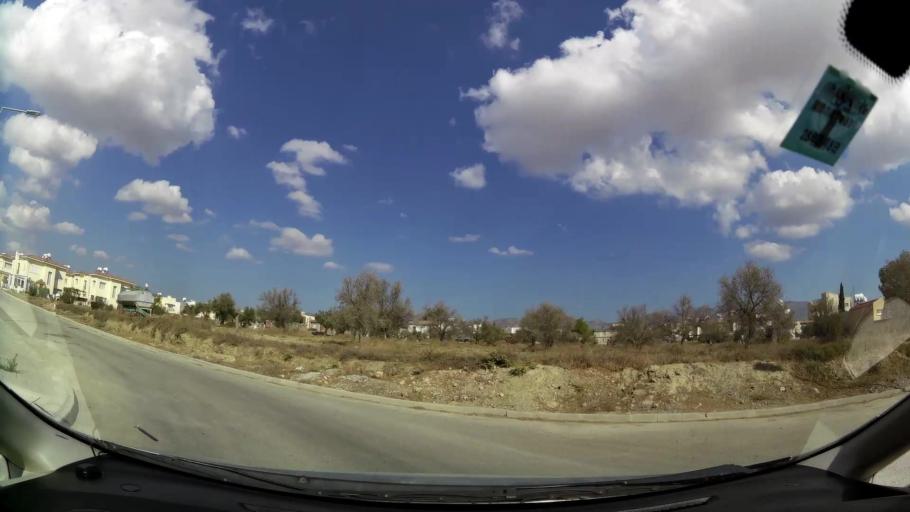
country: CY
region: Lefkosia
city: Nicosia
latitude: 35.2162
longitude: 33.3836
